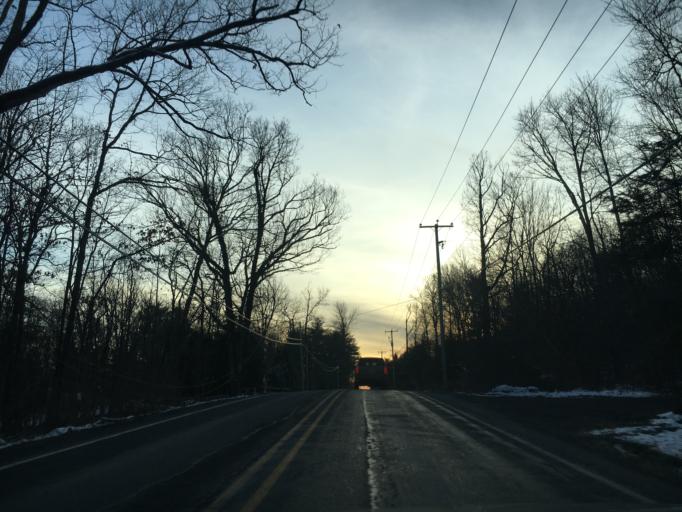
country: US
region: Pennsylvania
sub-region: Pike County
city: Saw Creek
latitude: 41.0803
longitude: -75.1050
